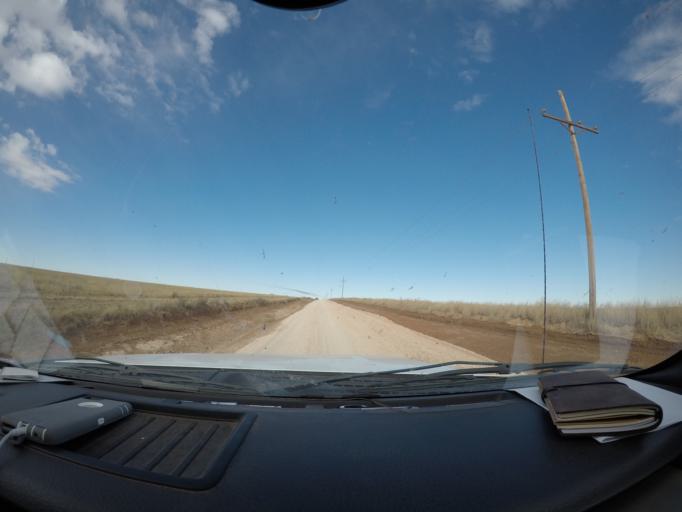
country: US
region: New Mexico
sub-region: Curry County
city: Texico
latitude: 34.6081
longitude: -103.0911
